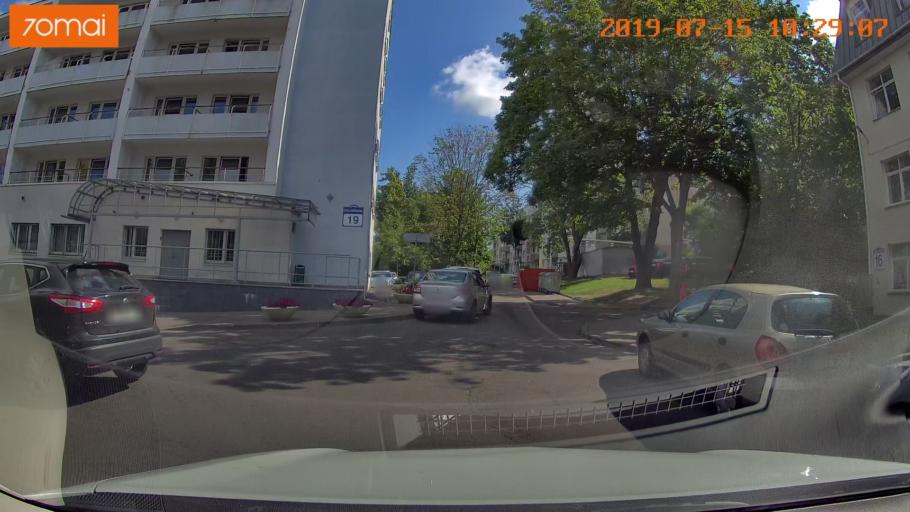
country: BY
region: Minsk
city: Minsk
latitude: 53.9113
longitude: 27.5866
